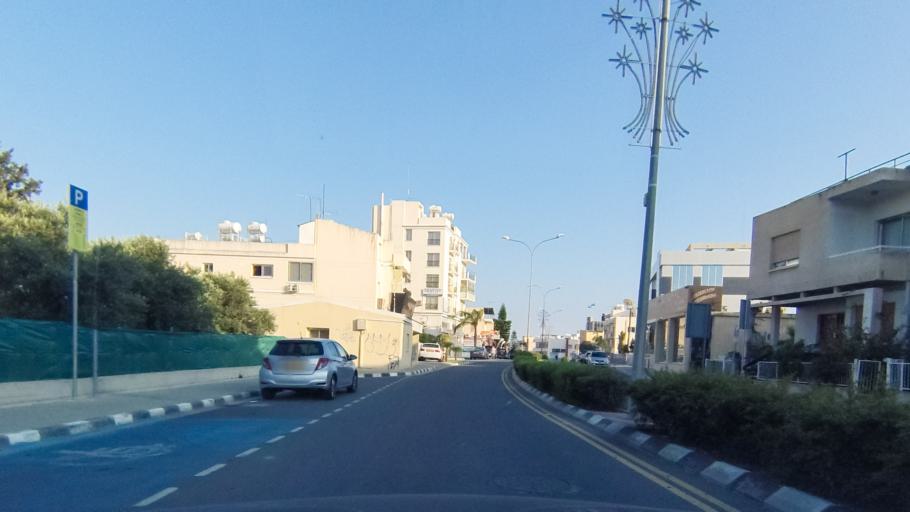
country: CY
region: Limassol
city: Mouttagiaka
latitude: 34.7065
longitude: 33.0861
